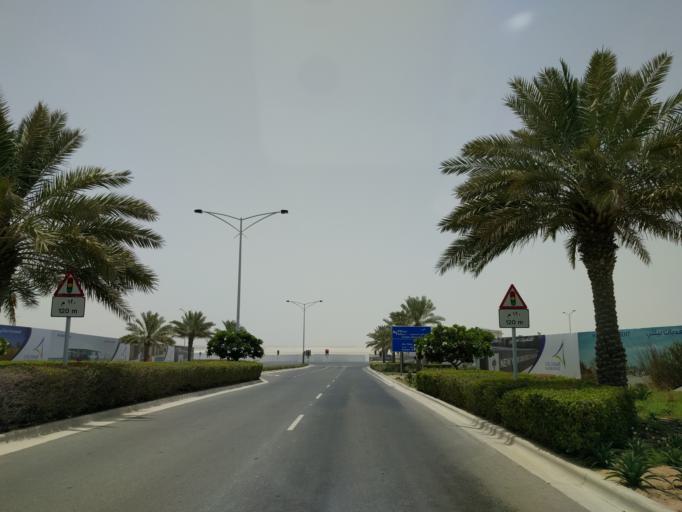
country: AE
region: Abu Dhabi
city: Abu Dhabi
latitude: 24.5421
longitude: 54.4419
